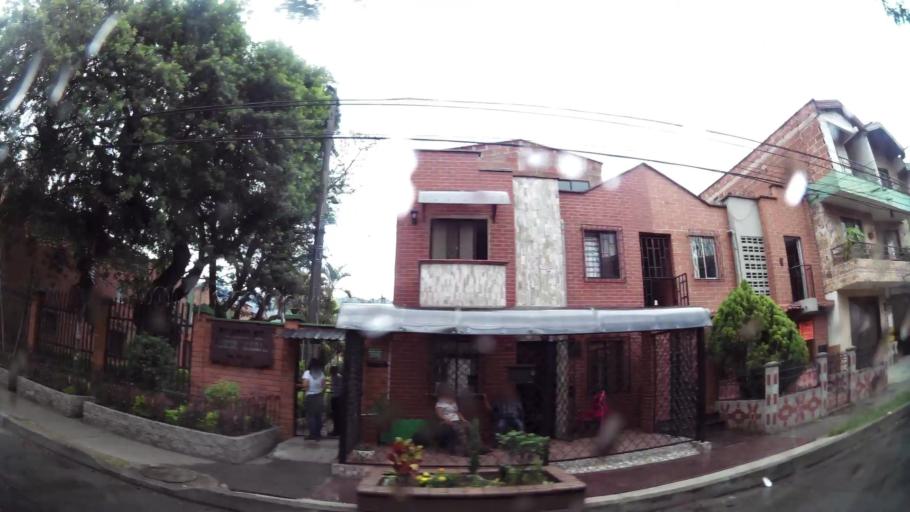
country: CO
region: Antioquia
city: Itagui
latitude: 6.1862
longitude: -75.5961
